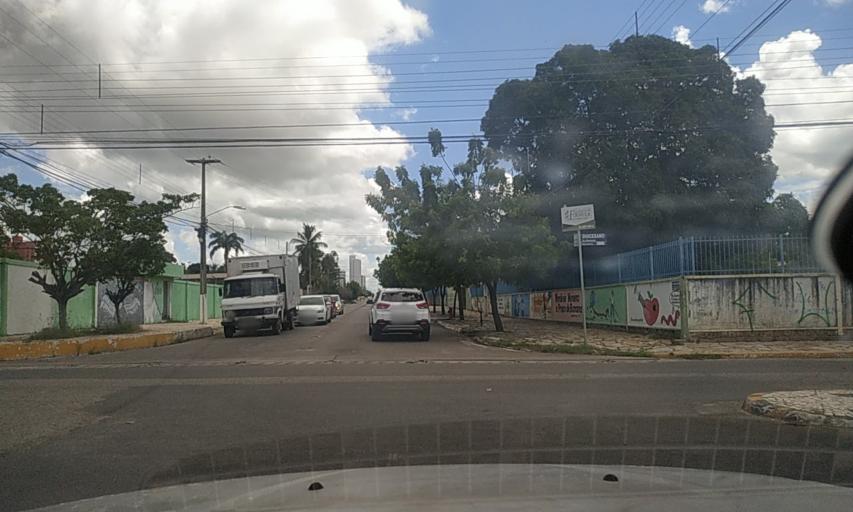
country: BR
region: Rio Grande do Norte
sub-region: Mossoro
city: Mossoro
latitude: -5.1851
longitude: -37.3518
